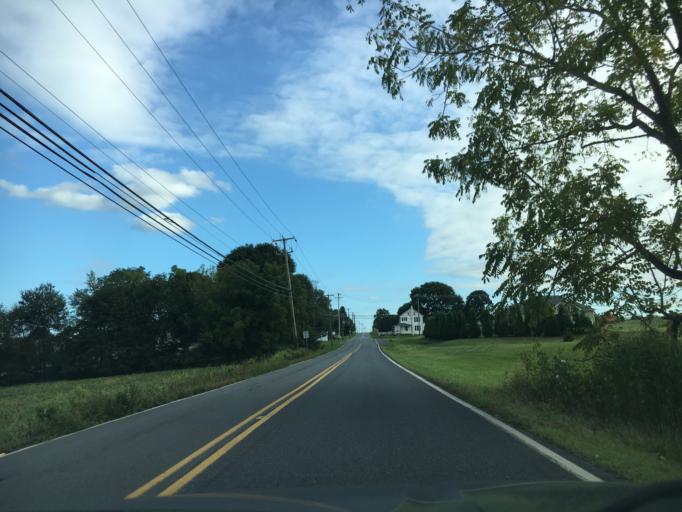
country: US
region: Pennsylvania
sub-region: Berks County
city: Topton
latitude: 40.5949
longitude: -75.7127
